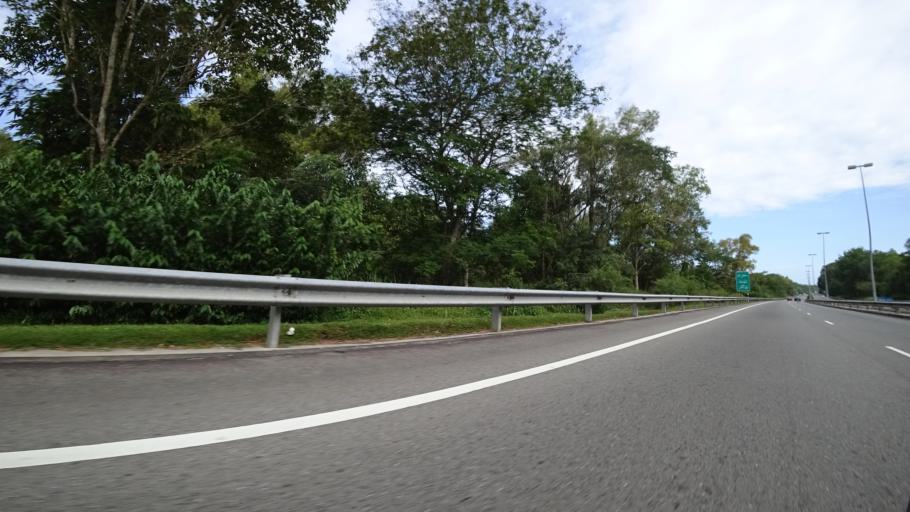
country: BN
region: Brunei and Muara
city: Bandar Seri Begawan
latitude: 4.9308
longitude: 114.9118
